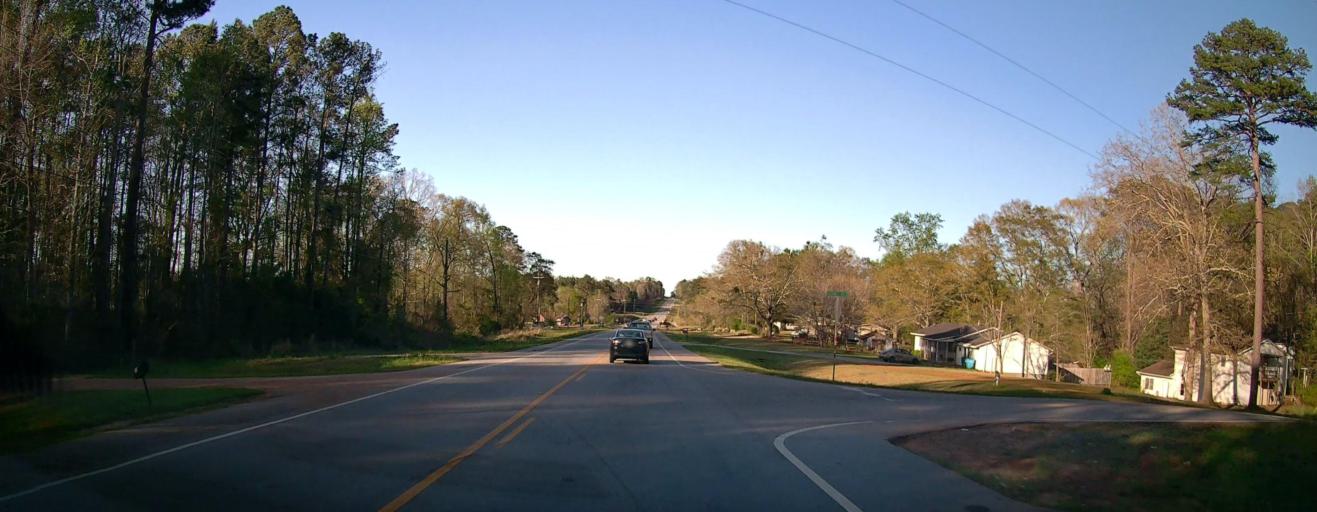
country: US
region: Georgia
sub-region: Butts County
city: Jackson
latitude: 33.3920
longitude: -83.8965
